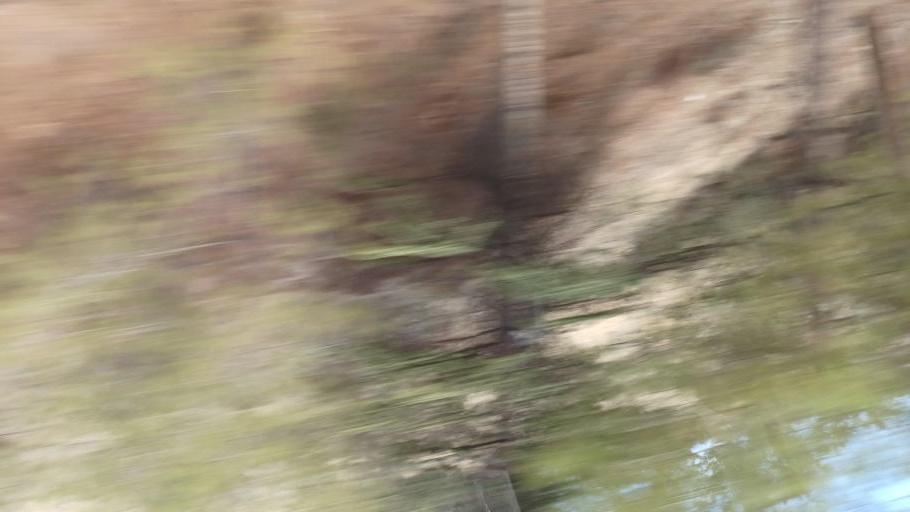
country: CY
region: Lefkosia
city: Kakopetria
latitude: 34.9827
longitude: 32.9066
